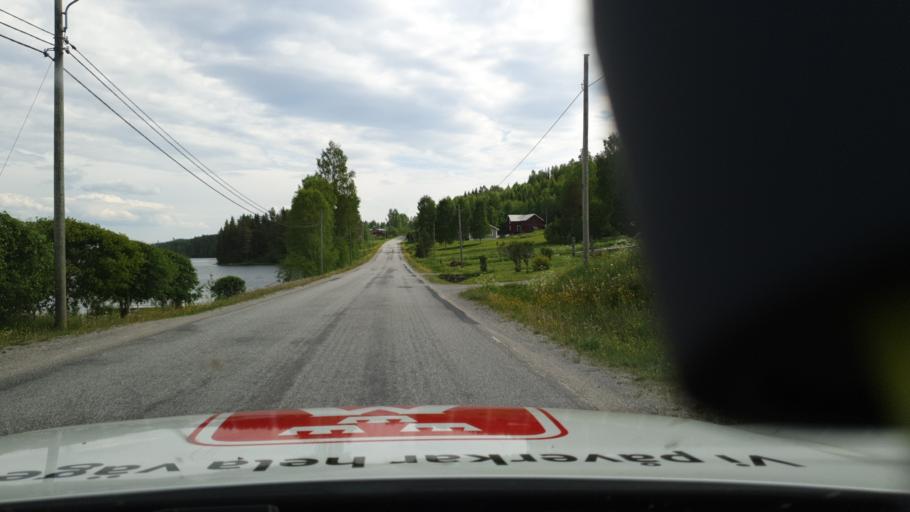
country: SE
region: Jaemtland
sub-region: Braecke Kommun
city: Braecke
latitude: 62.9886
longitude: 15.2022
